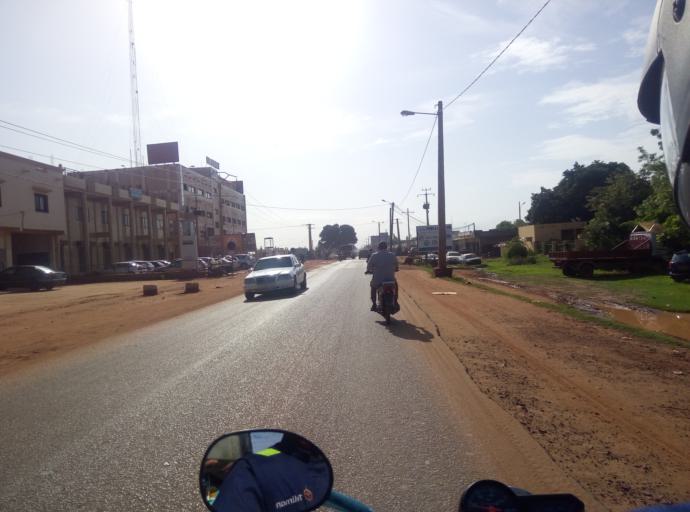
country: ML
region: Bamako
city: Bamako
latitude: 12.6519
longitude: -7.9485
